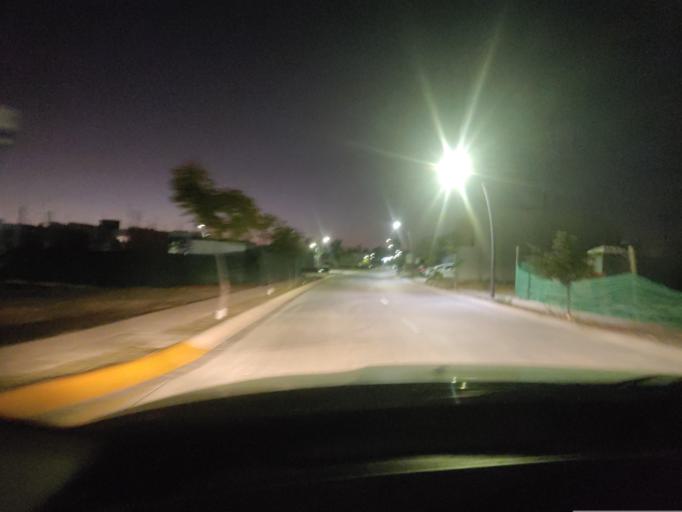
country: MX
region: Guanajuato
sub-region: Leon
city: Ladrilleras del Refugio
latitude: 21.0851
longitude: -101.5589
